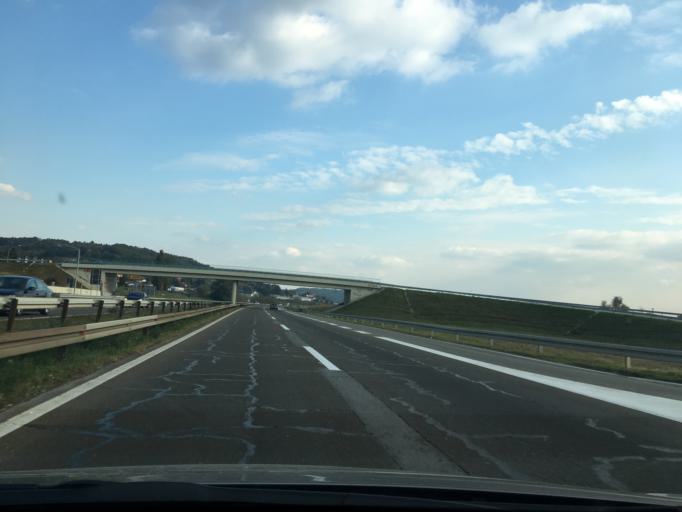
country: RS
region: Central Serbia
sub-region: Belgrade
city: Zvezdara
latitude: 44.7048
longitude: 20.5734
